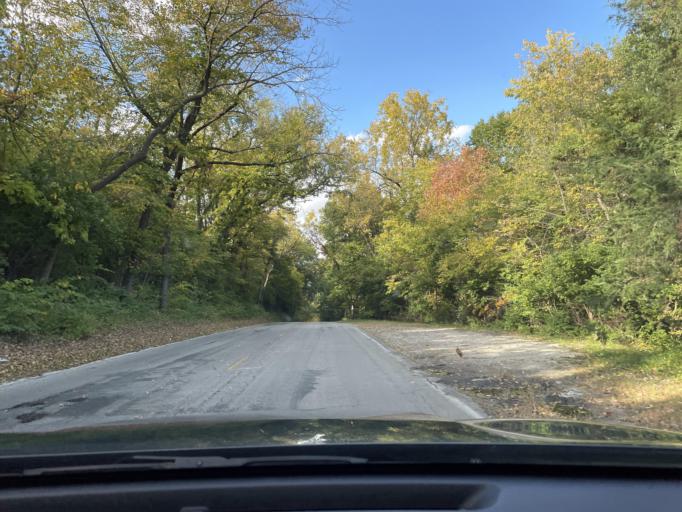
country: US
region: Missouri
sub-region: Buchanan County
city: Saint Joseph
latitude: 39.7300
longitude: -94.8384
